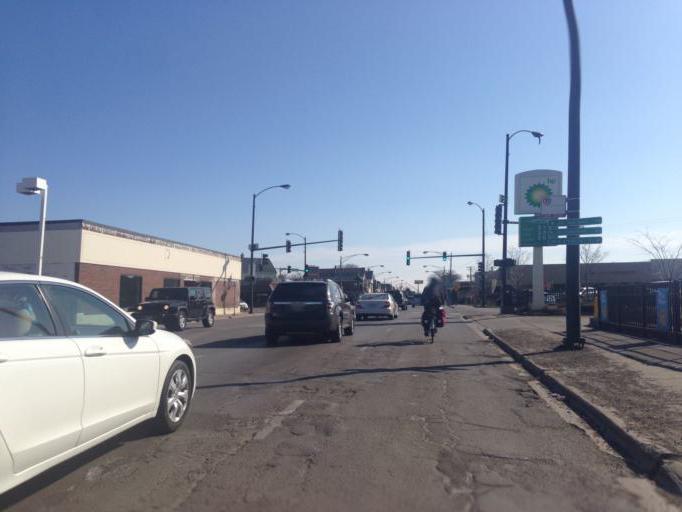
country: US
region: Illinois
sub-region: Cook County
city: Lincolnwood
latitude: 41.9465
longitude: -87.7079
